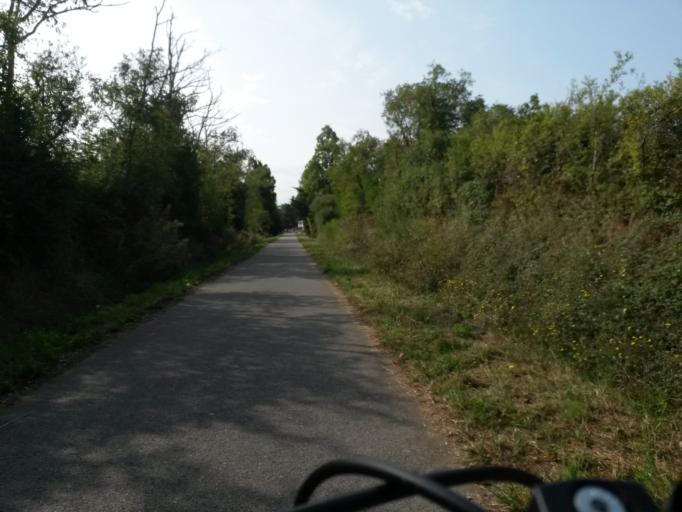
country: FR
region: Pays de la Loire
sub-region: Departement de la Loire-Atlantique
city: La Baule-Escoublac
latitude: 47.2935
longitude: -2.3950
